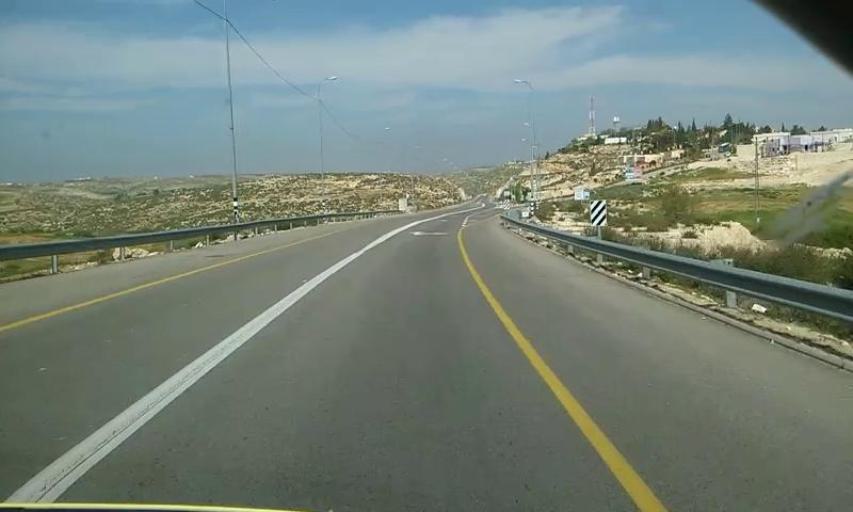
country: PS
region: West Bank
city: Az Zahiriyah
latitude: 31.3854
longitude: 35.0067
